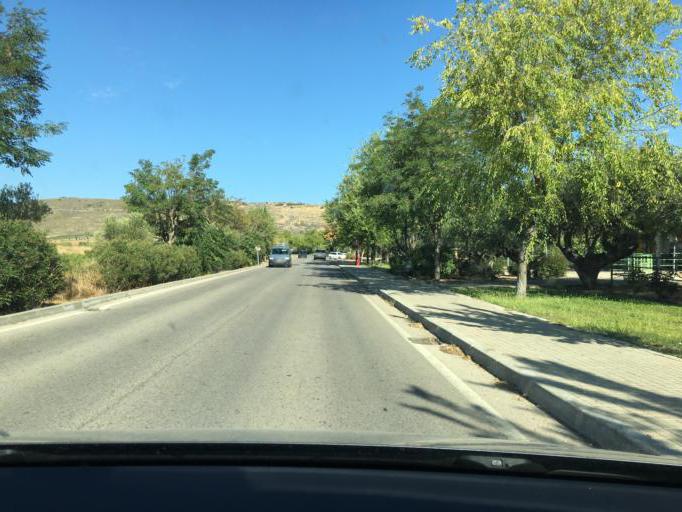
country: ES
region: Madrid
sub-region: Provincia de Madrid
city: Torremocha de Jarama
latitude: 40.8391
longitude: -3.5007
